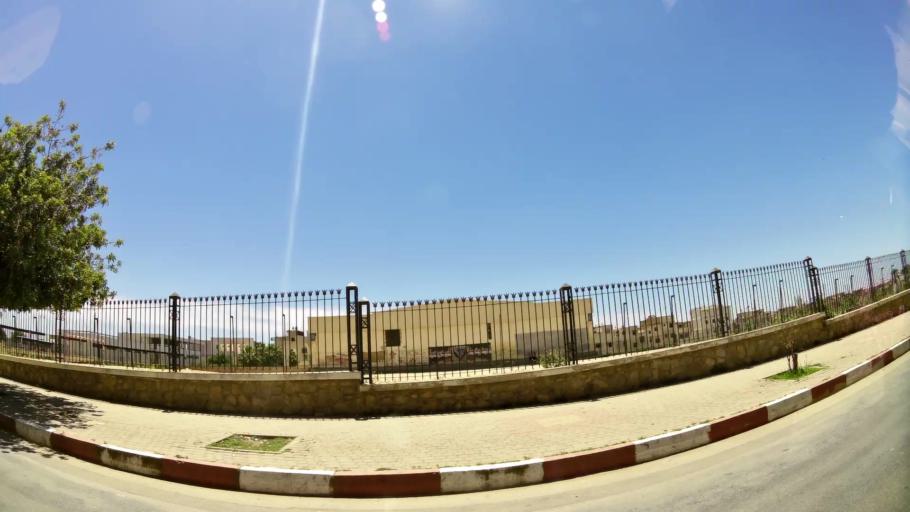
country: MA
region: Meknes-Tafilalet
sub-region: Meknes
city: Meknes
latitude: 33.9049
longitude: -5.5731
